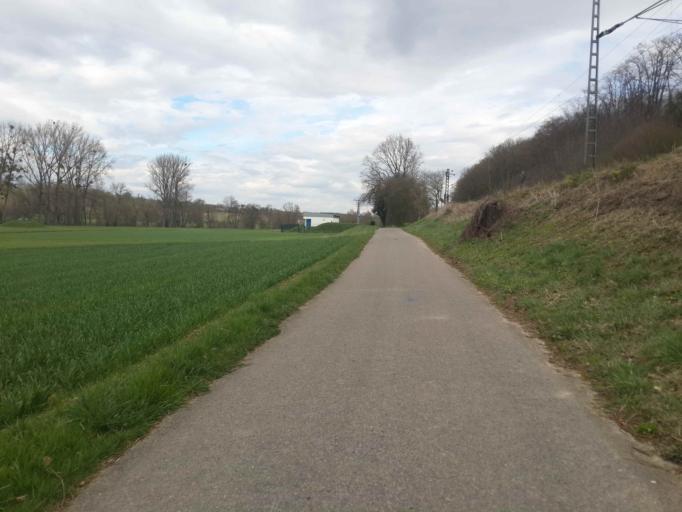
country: DE
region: Baden-Wuerttemberg
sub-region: Regierungsbezirk Stuttgart
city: Untereisesheim
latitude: 49.2449
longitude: 9.1975
